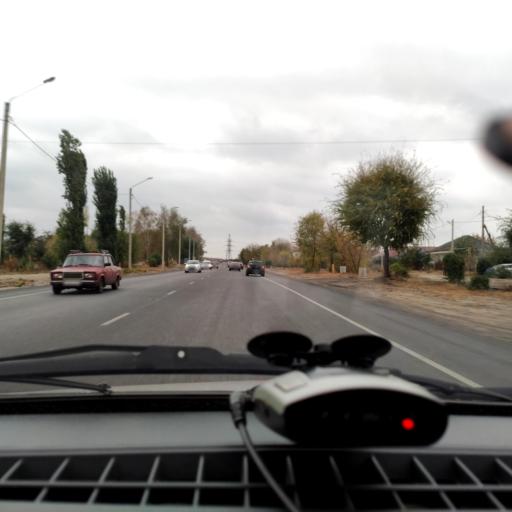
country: RU
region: Voronezj
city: Pridonskoy
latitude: 51.7026
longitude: 39.0771
